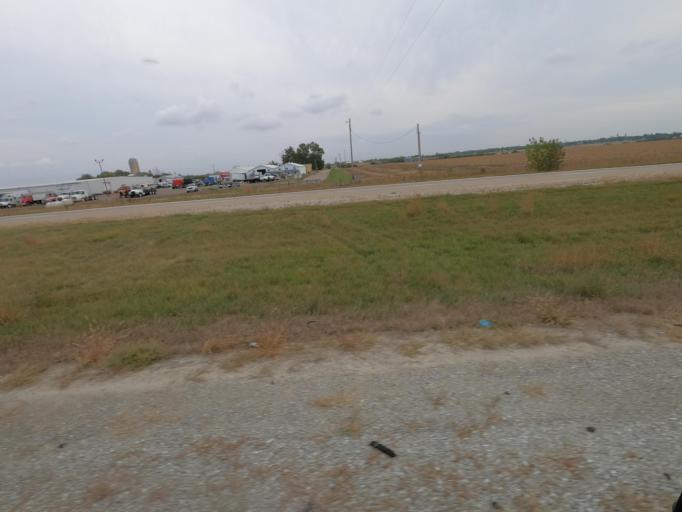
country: US
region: Iowa
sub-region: Jasper County
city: Monroe
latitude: 41.5371
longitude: -93.1304
